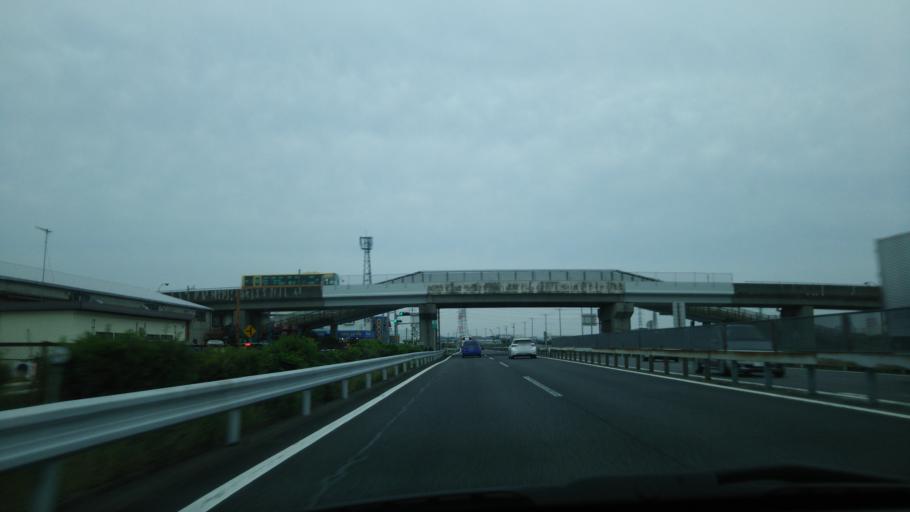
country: JP
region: Kanagawa
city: Isehara
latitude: 35.3902
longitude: 139.3329
